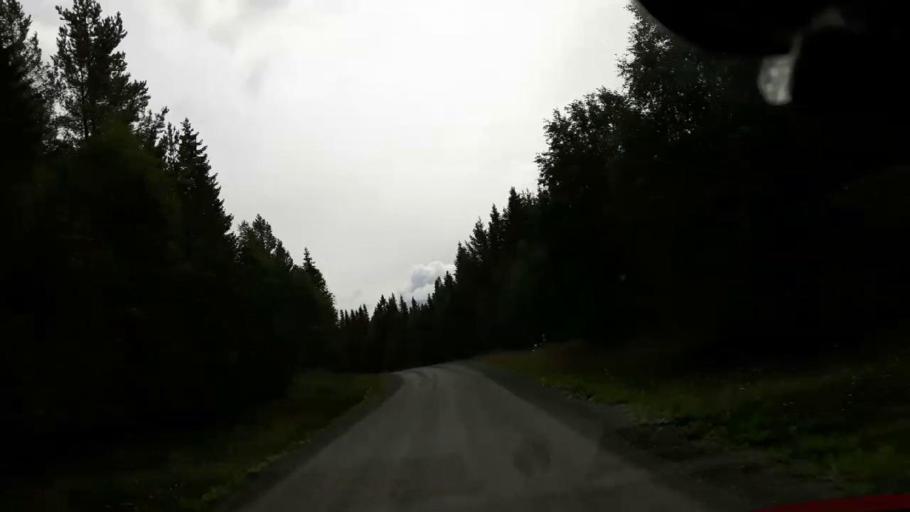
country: SE
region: Jaemtland
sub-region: Krokoms Kommun
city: Valla
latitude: 63.6628
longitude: 13.9681
